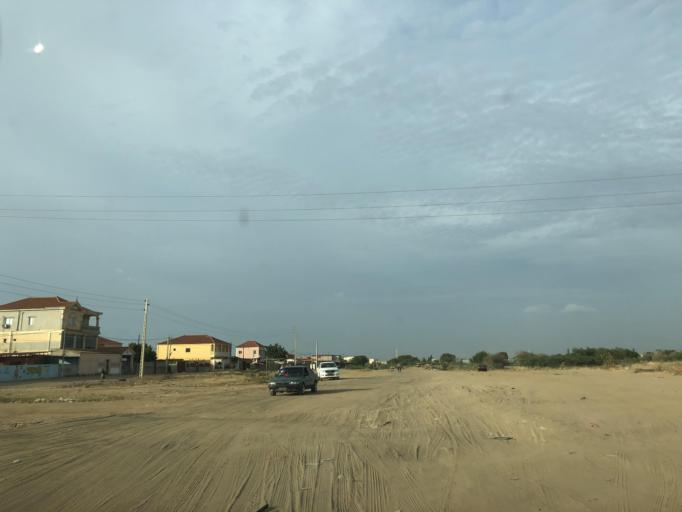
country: AO
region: Luanda
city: Luanda
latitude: -8.9124
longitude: 13.3142
